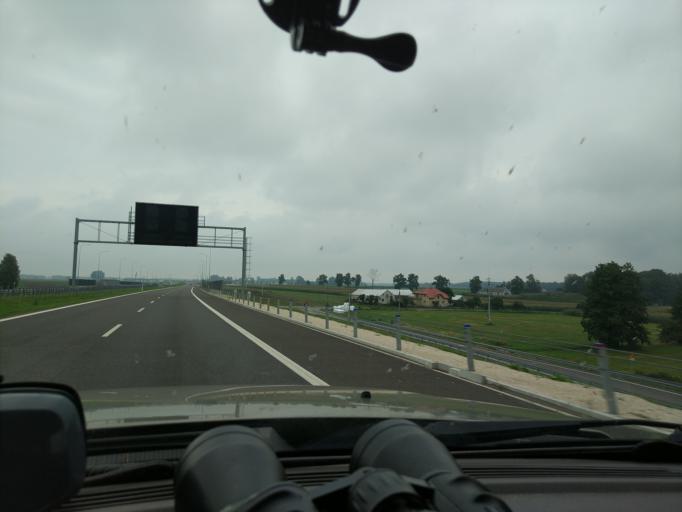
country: PL
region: Podlasie
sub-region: Powiat zambrowski
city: Szumowo
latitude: 52.9456
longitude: 22.1581
